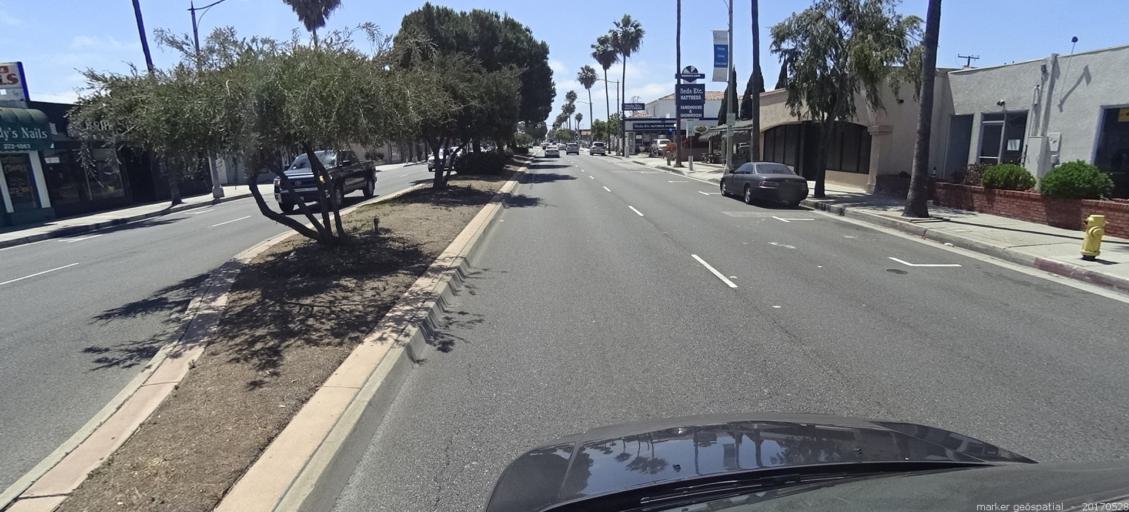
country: US
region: California
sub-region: Los Angeles County
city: Lawndale
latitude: 33.8729
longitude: -118.3667
